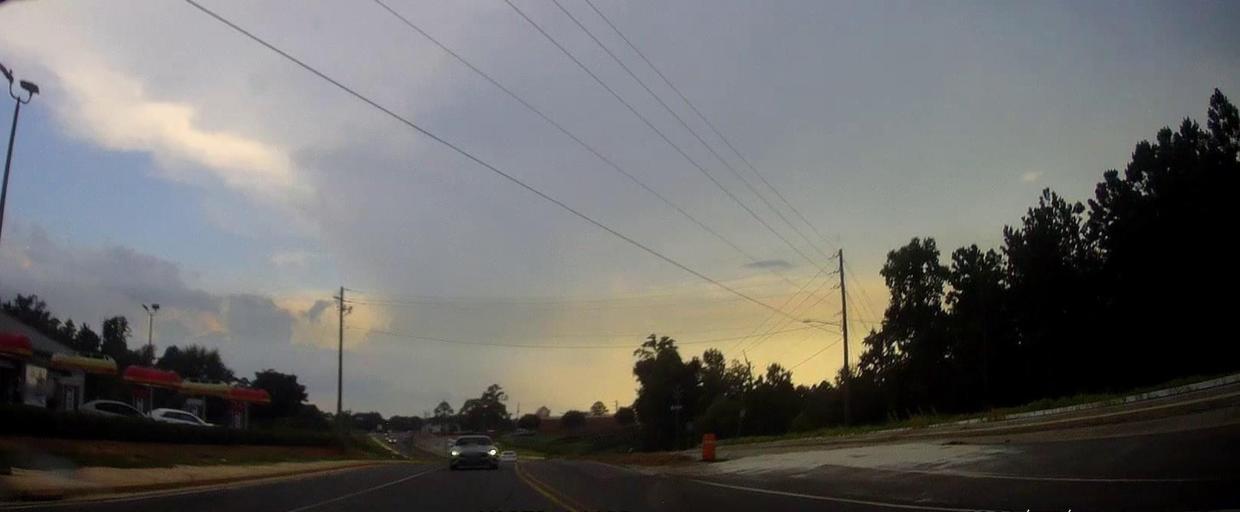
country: US
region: Georgia
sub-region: Laurens County
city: Dublin
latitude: 32.5448
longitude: -82.9418
